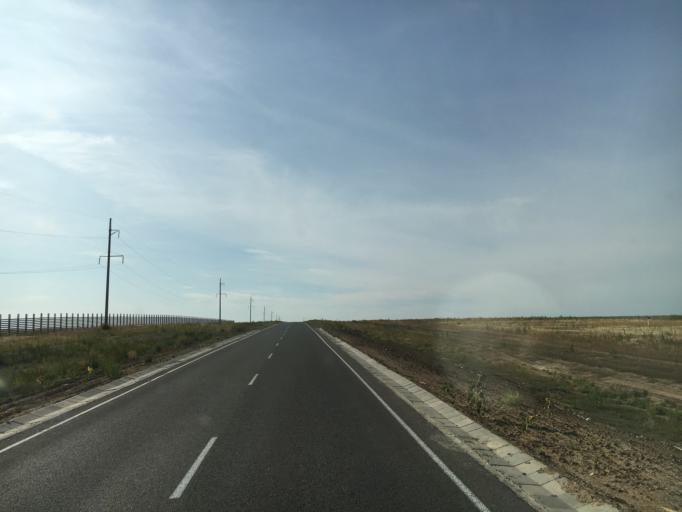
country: KZ
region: Batys Qazaqstan
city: Kamenka
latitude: 51.1438
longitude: 50.0980
